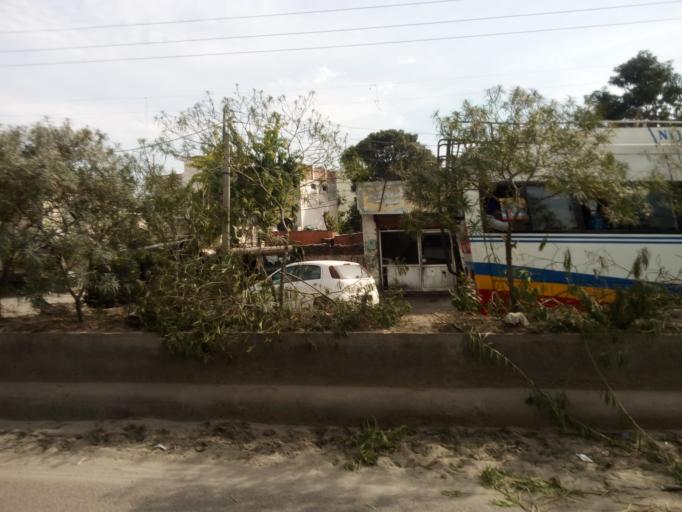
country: IN
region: Punjab
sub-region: Hoshiarpur
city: Hoshiarpur
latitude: 31.5323
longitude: 75.9001
